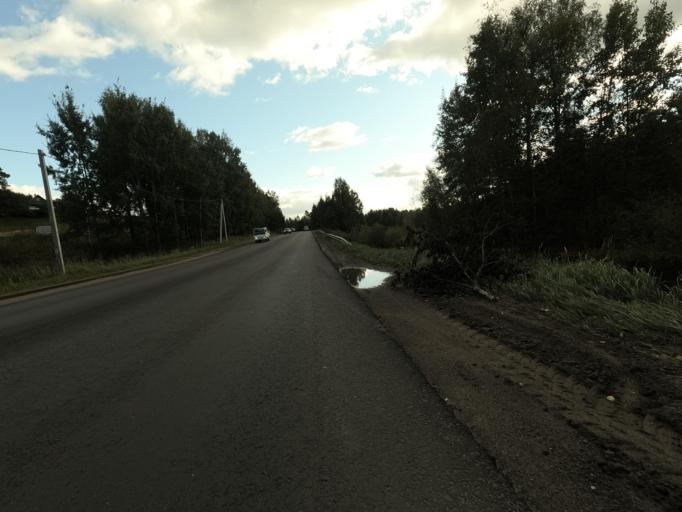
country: RU
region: Leningrad
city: Koltushi
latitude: 59.9734
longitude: 30.6532
